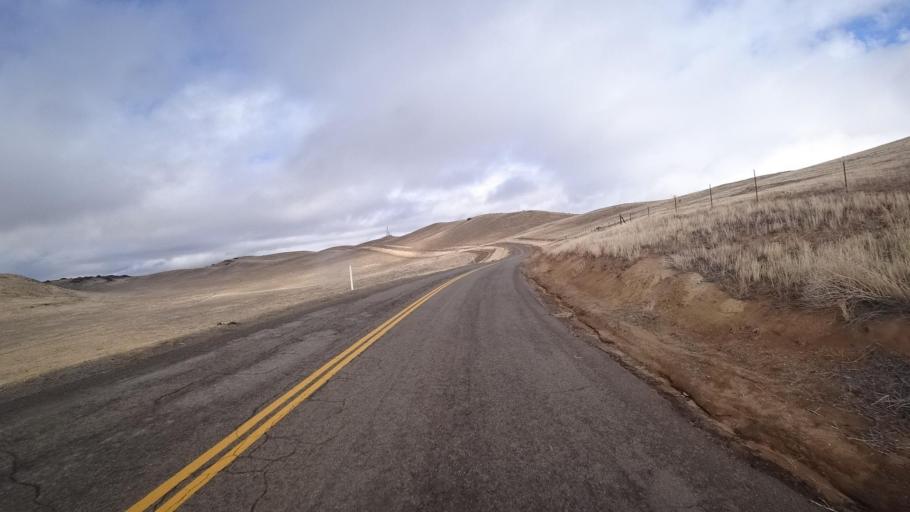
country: US
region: California
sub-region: Kern County
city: Maricopa
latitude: 34.9081
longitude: -119.3936
